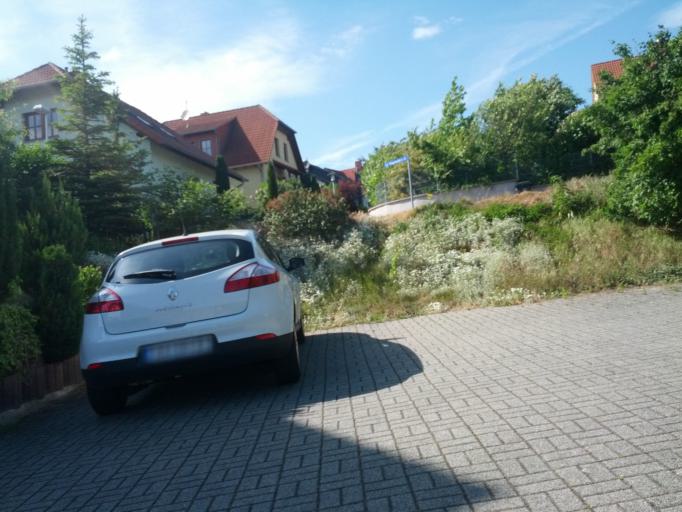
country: DE
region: Thuringia
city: Eisenach
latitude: 51.0081
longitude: 10.3061
